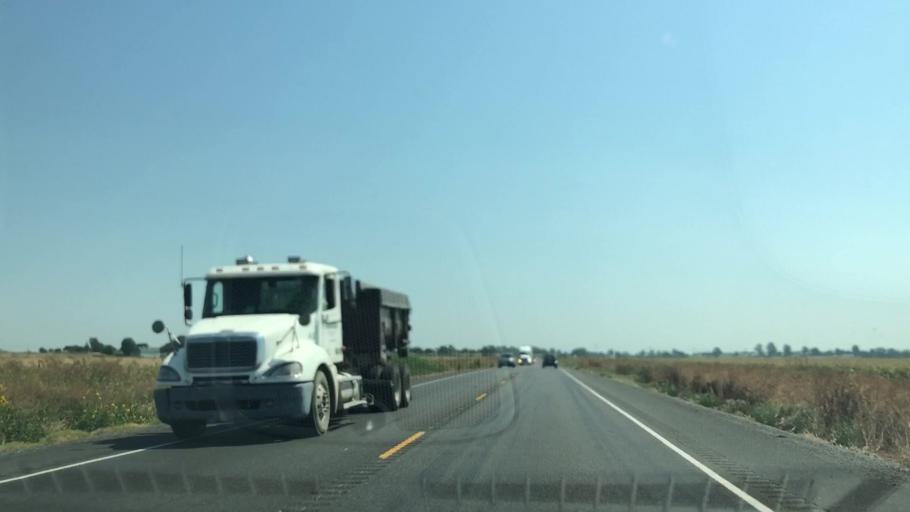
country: US
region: California
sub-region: Solano County
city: Rio Vista
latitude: 38.1343
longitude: -121.6033
